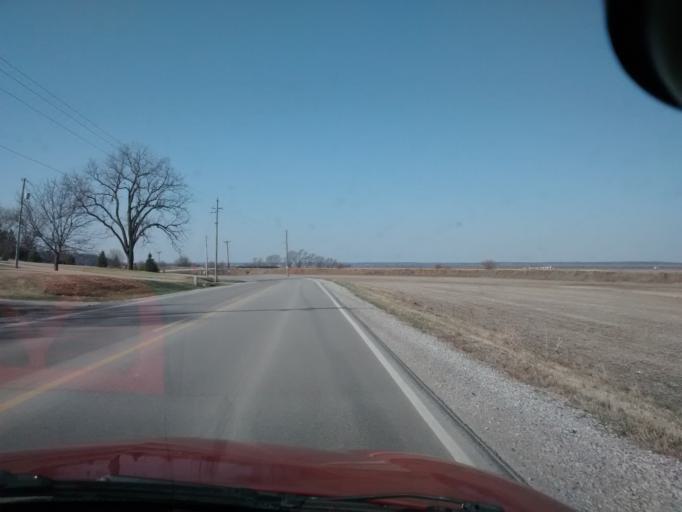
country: US
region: Iowa
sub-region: Pottawattamie County
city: Carter Lake
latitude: 41.3788
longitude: -95.8544
